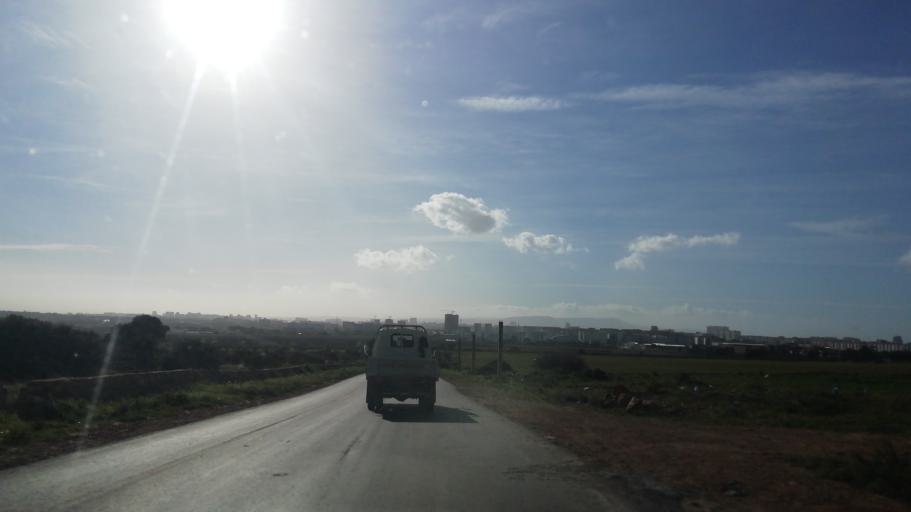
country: DZ
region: Oran
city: Bir el Djir
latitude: 35.7525
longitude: -0.5155
